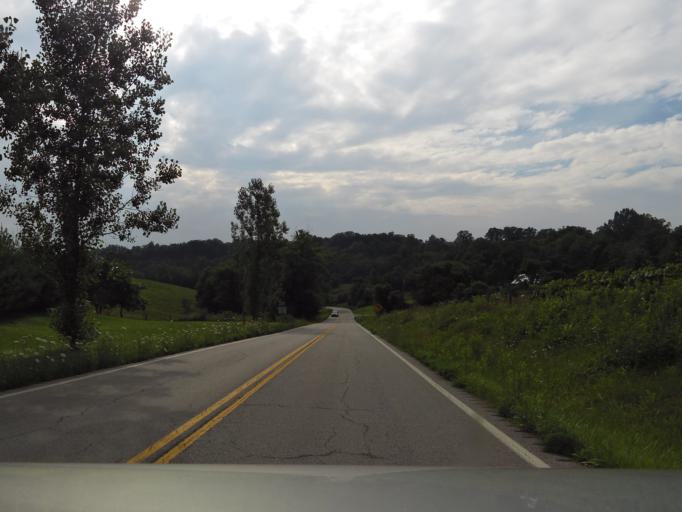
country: US
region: Kentucky
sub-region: Robertson County
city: Mount Olivet
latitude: 38.5242
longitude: -84.1693
